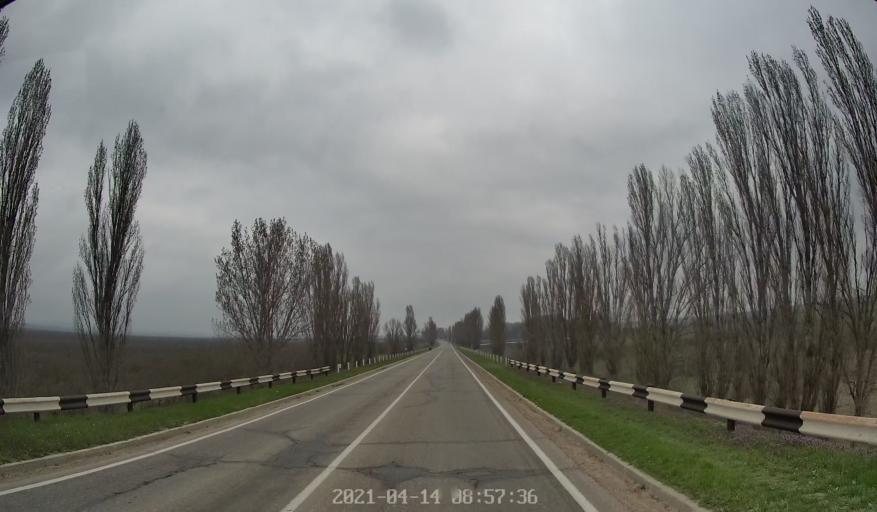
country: MD
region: Chisinau
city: Vadul lui Voda
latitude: 47.0934
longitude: 29.0939
